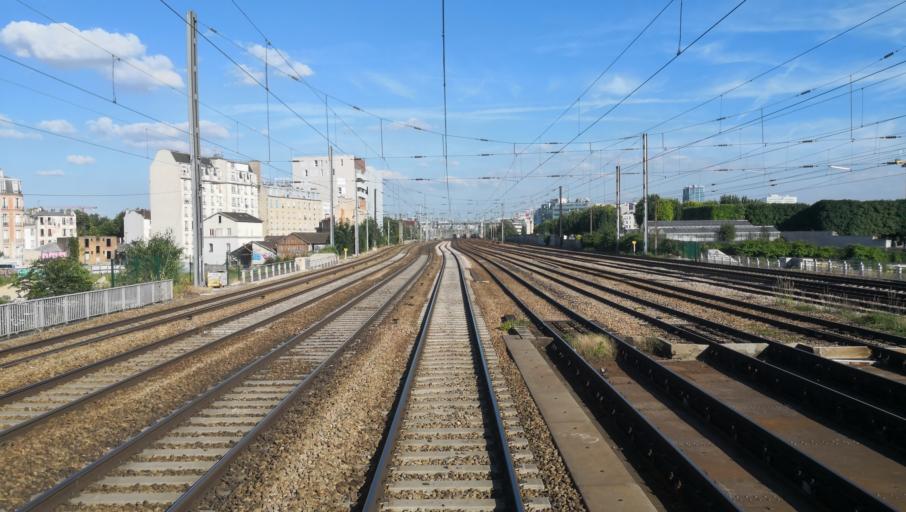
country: FR
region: Ile-de-France
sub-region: Departement des Hauts-de-Seine
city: Levallois-Perret
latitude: 48.9033
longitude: 2.2880
